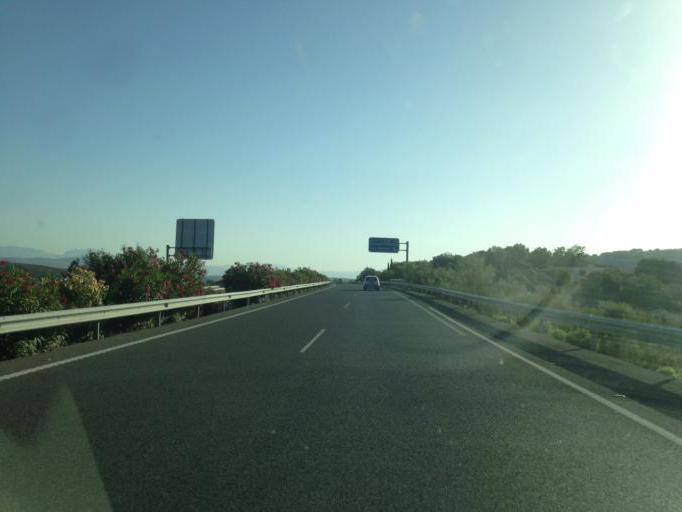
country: ES
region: Andalusia
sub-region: Provincia de Malaga
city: Villanueva de Tapia
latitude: 37.1199
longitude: -4.2947
